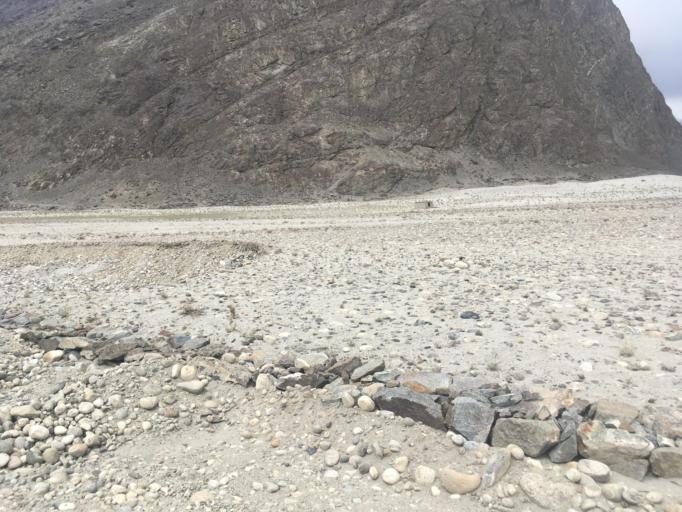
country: PK
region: Gilgit-Baltistan
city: Skardu
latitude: 35.3137
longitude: 75.6578
